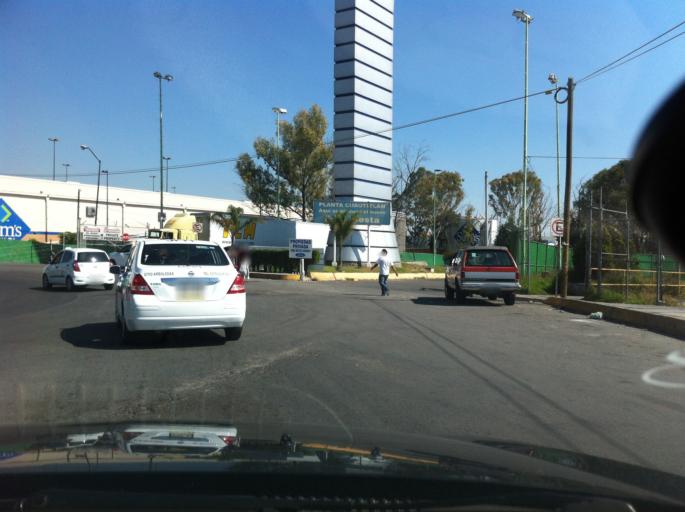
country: MX
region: Mexico
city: Cuautitlan Izcalli
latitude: 19.6446
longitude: -99.1946
